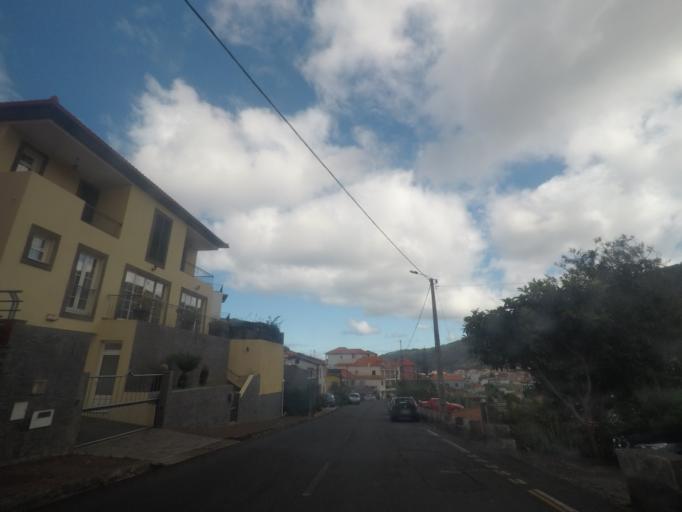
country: PT
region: Madeira
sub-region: Machico
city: Machico
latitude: 32.7289
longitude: -16.7712
